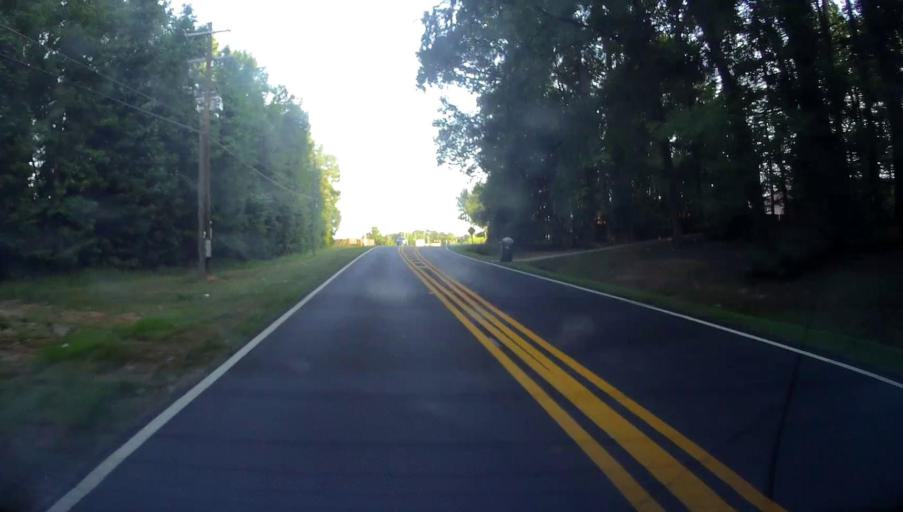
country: US
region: Georgia
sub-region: Bibb County
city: Macon
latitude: 32.9014
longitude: -83.7041
